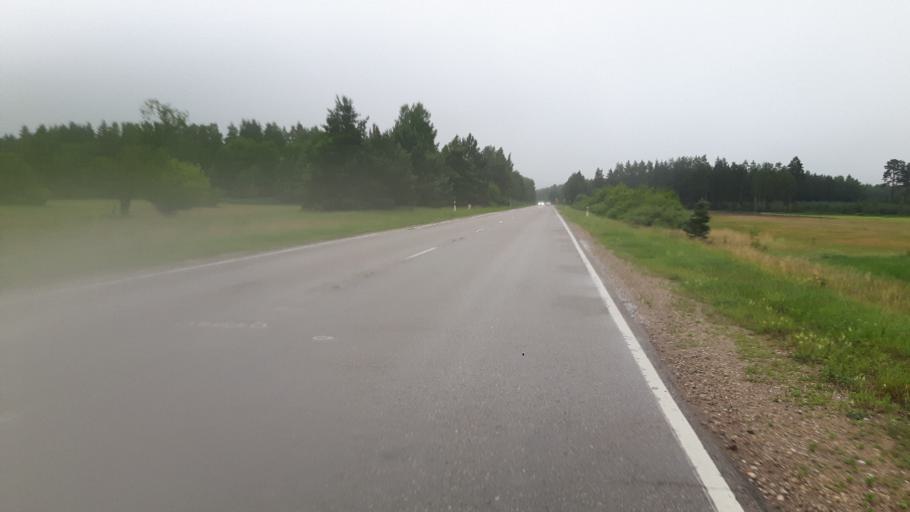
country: LV
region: Rucavas
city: Rucava
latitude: 56.1029
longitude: 21.1351
